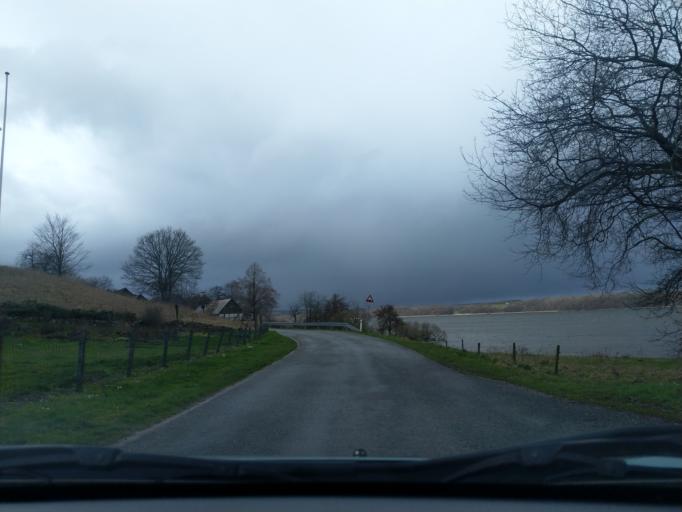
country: DK
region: Zealand
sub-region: Soro Kommune
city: Frederiksberg
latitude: 55.3618
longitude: 11.5687
